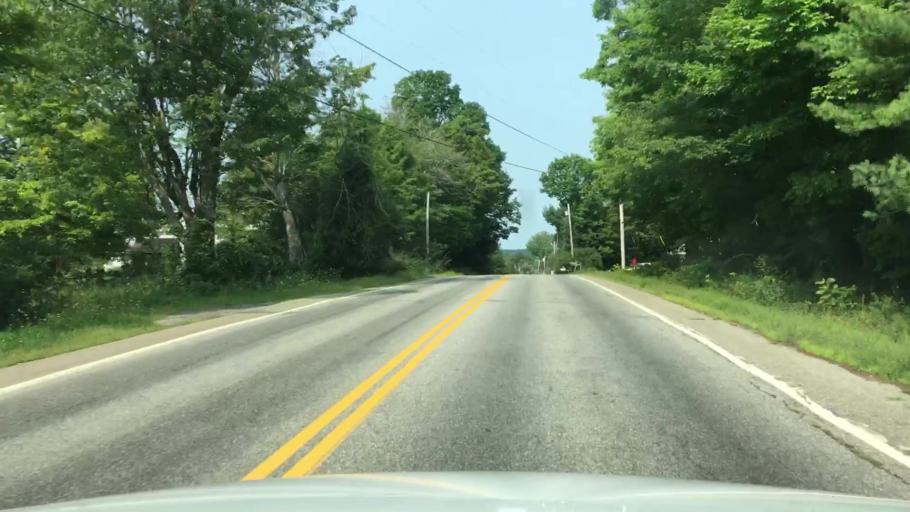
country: US
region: Maine
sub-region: Kennebec County
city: Augusta
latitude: 44.3183
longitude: -69.7376
